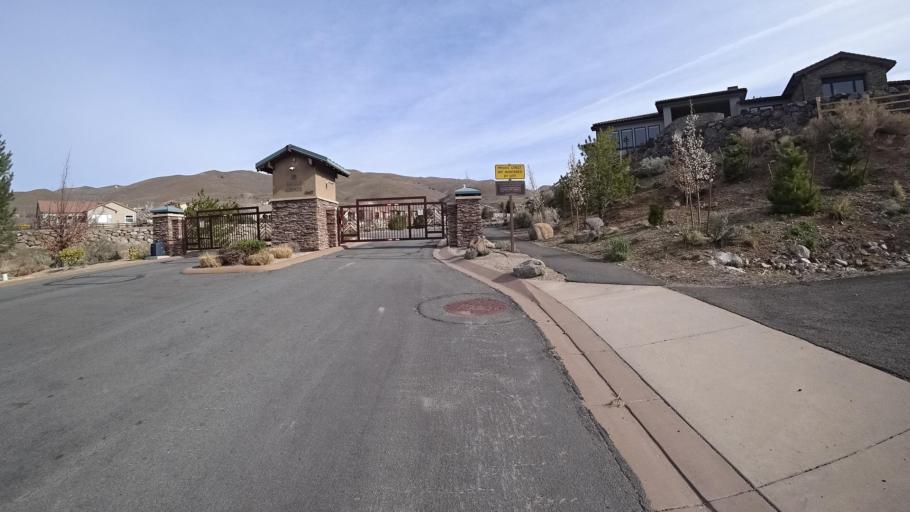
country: US
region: Nevada
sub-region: Washoe County
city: Mogul
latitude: 39.5372
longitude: -119.9359
